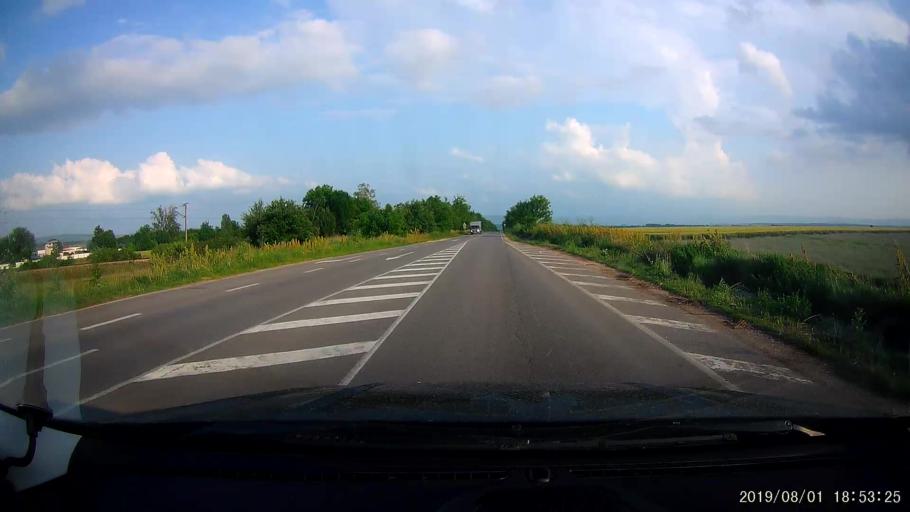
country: BG
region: Shumen
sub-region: Obshtina Shumen
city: Shumen
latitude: 43.2214
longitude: 26.9933
